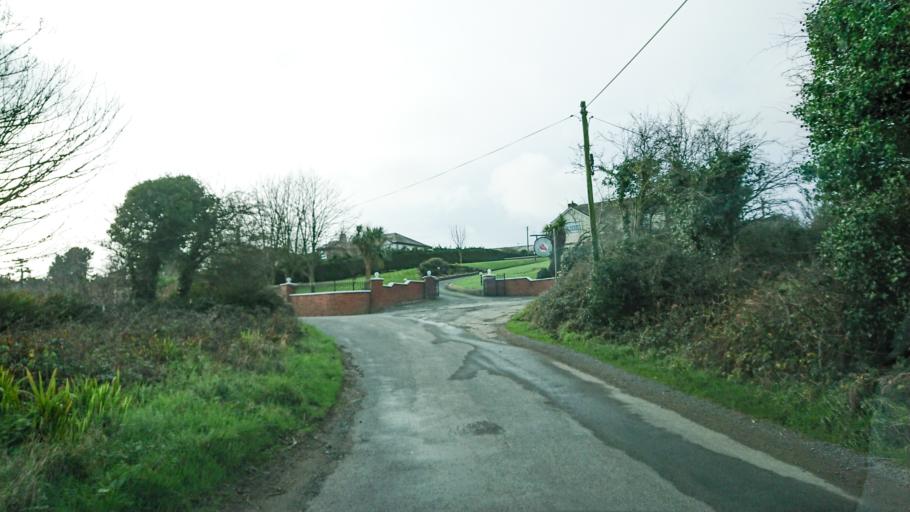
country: IE
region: Munster
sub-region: Waterford
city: Tra Mhor
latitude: 52.1785
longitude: -7.1750
